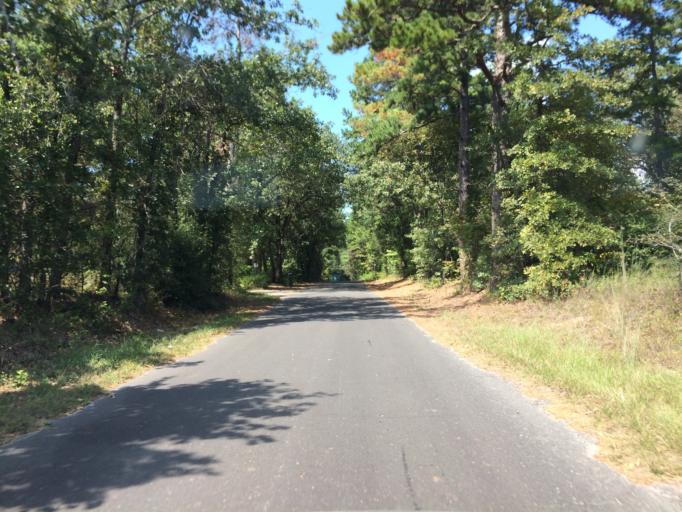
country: US
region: Texas
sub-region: Wood County
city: Hawkins
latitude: 32.7318
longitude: -95.1921
